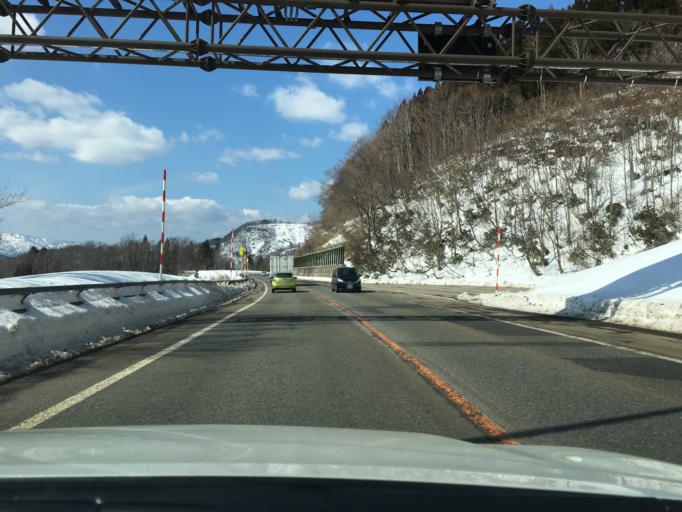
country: JP
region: Yamagata
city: Tsuruoka
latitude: 38.5660
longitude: 139.9388
